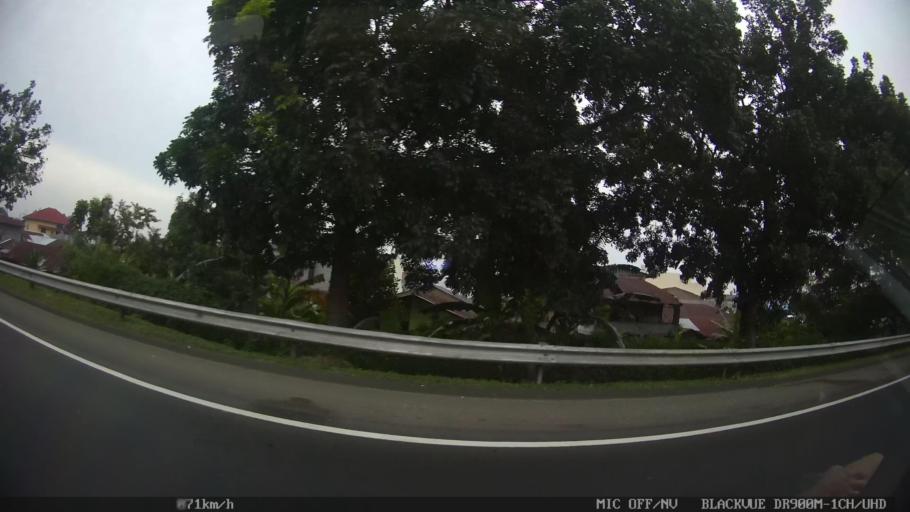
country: ID
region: North Sumatra
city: Medan
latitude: 3.5784
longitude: 98.7248
